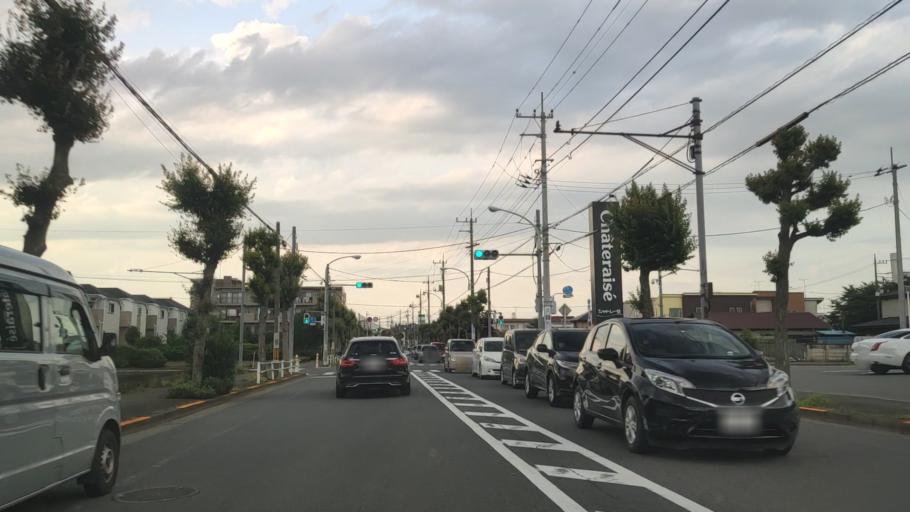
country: JP
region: Tokyo
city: Ome
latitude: 35.7897
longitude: 139.2929
